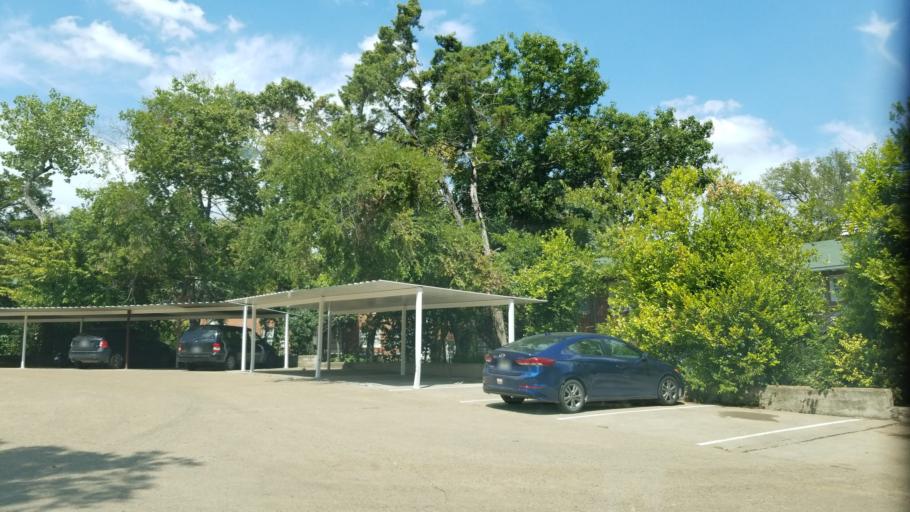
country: US
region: Texas
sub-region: Dallas County
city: Cockrell Hill
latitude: 32.7623
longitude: -96.8524
